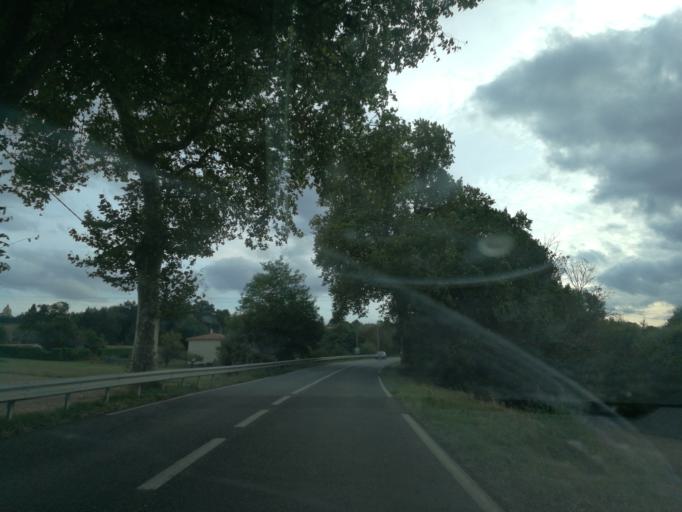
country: FR
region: Midi-Pyrenees
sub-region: Departement de la Haute-Garonne
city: Dremil-Lafage
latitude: 43.5898
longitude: 1.5862
